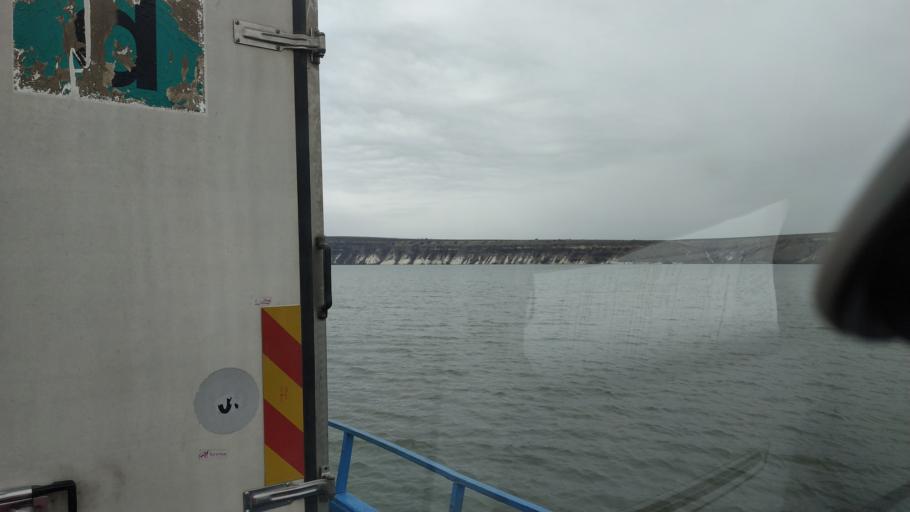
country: MD
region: Telenesti
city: Cocieri
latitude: 47.3507
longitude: 29.1000
